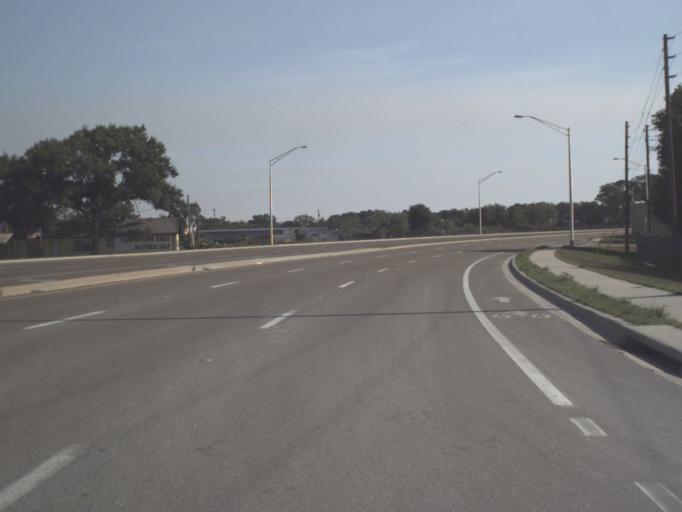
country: US
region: Florida
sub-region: Orange County
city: Lockhart
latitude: 28.6066
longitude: -81.4183
